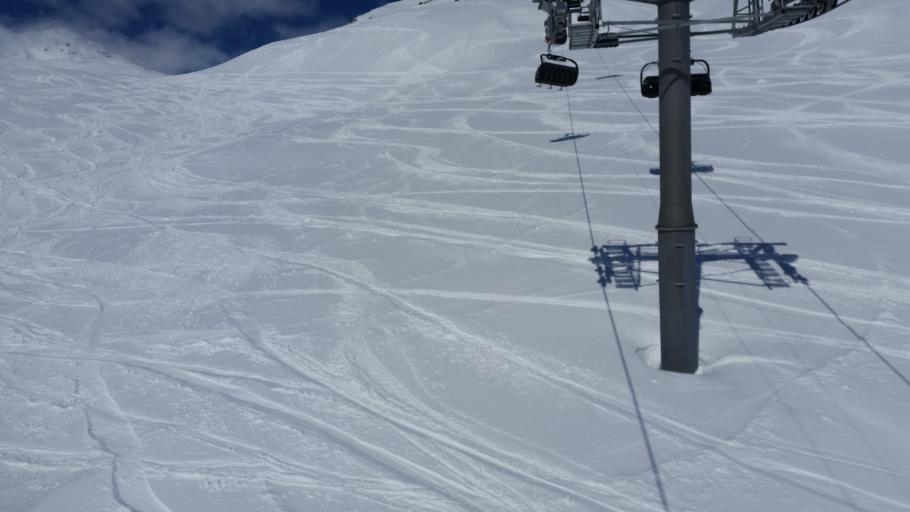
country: CH
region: Grisons
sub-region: Surselva District
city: Ilanz
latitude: 46.8515
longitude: 9.1623
